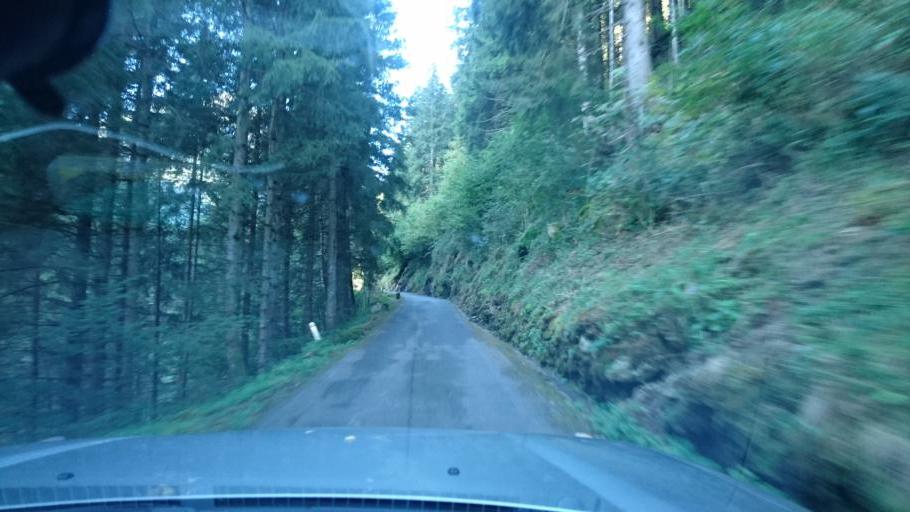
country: IT
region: Lombardy
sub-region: Provincia di Brescia
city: Paisco Loveno
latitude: 46.0566
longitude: 10.2415
